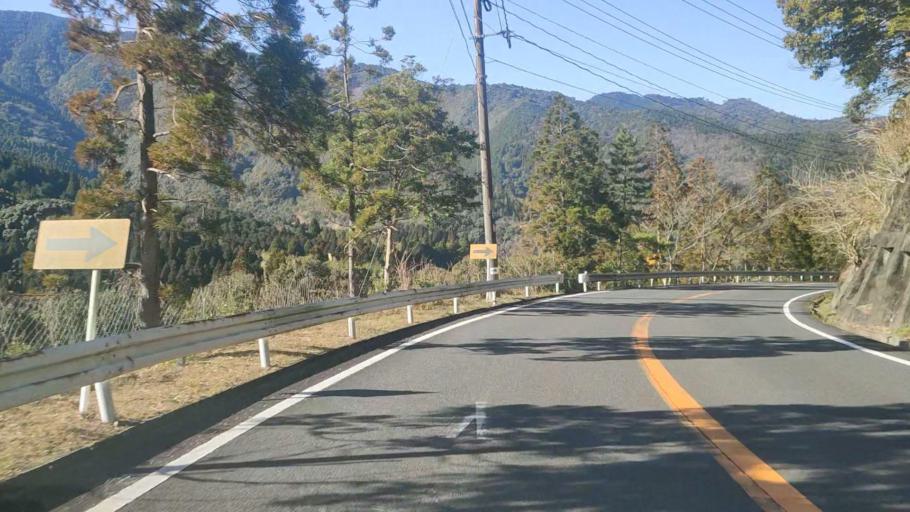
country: JP
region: Oita
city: Saiki
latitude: 32.8955
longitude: 131.9390
